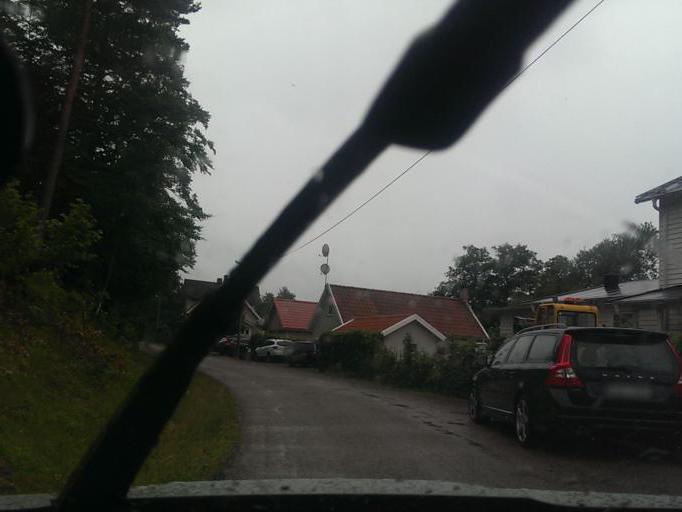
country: SE
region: Skane
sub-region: Orkelljunga Kommun
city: OErkelljunga
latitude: 56.3049
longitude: 13.3774
